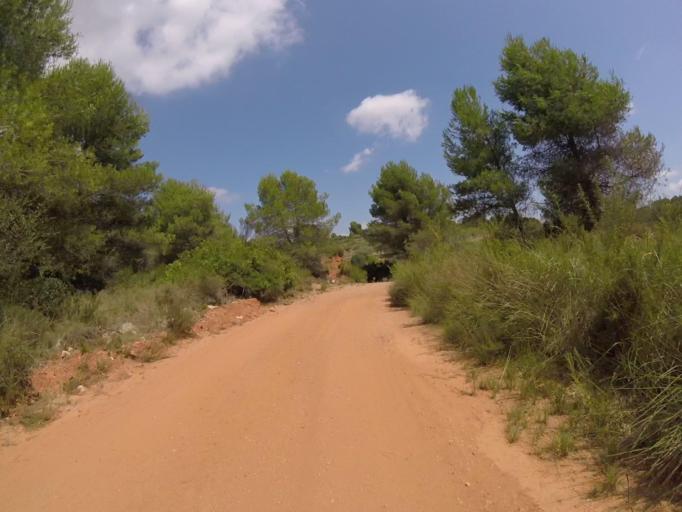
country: ES
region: Valencia
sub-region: Provincia de Castello
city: Torreblanca
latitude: 40.2065
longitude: 0.1367
